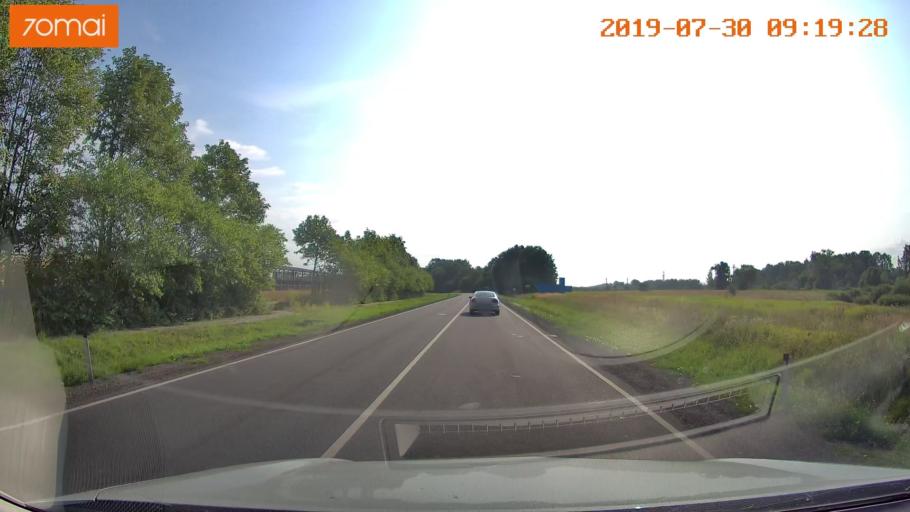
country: RU
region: Kaliningrad
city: Nesterov
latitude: 54.6323
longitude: 22.5911
